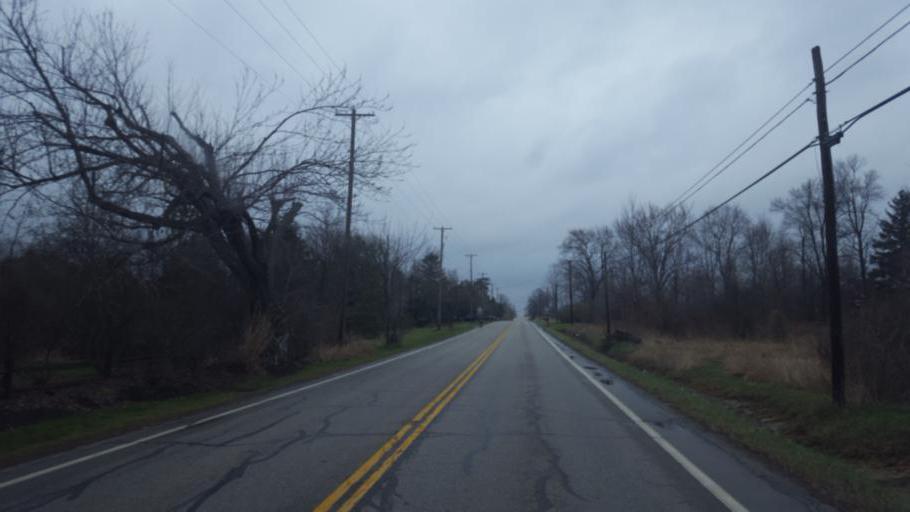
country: US
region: Ohio
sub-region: Medina County
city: Medina
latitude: 41.0924
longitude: -81.8642
